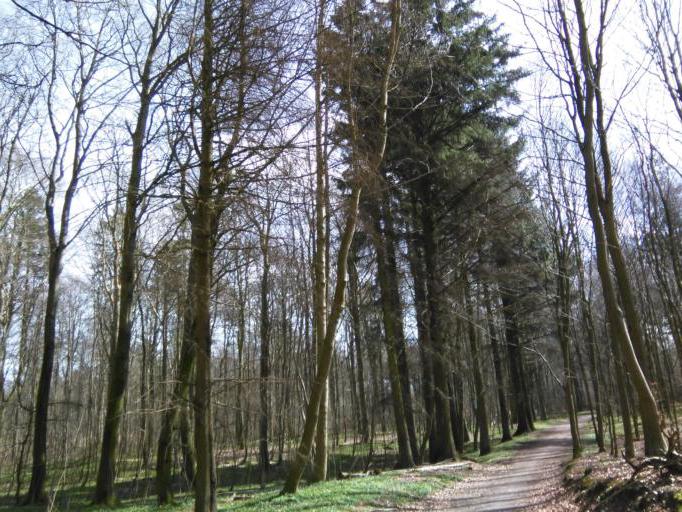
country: DK
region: Central Jutland
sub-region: Arhus Kommune
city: Beder
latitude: 56.1020
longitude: 10.2258
